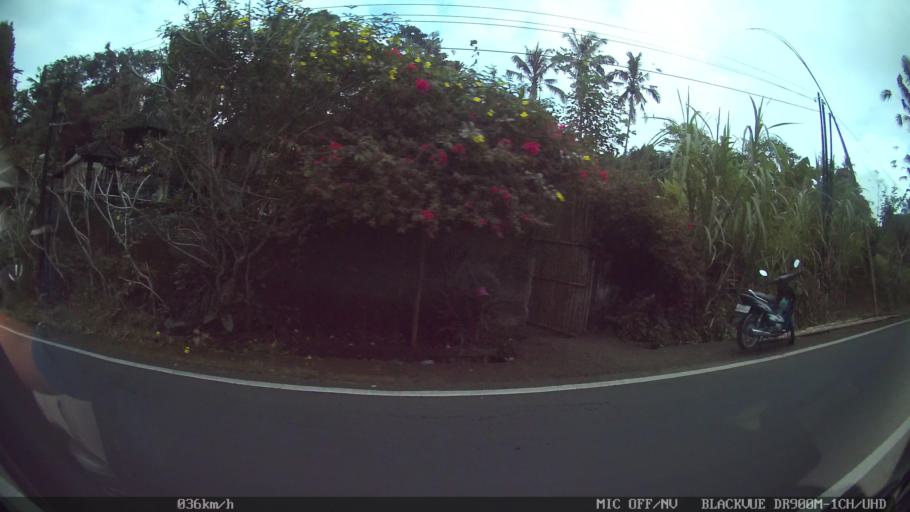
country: ID
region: Bali
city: Banjar Kubu
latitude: -8.4472
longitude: 115.3987
